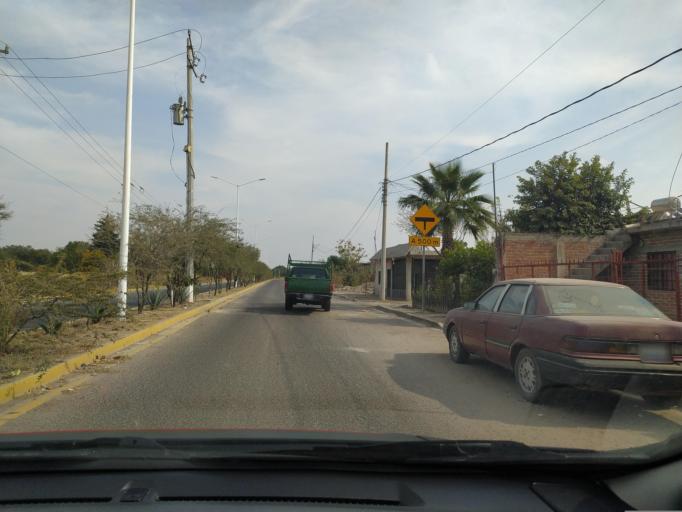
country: MX
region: Guanajuato
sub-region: San Francisco del Rincon
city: Fraccionamiento la Mezquitera
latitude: 21.0172
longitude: -101.8323
